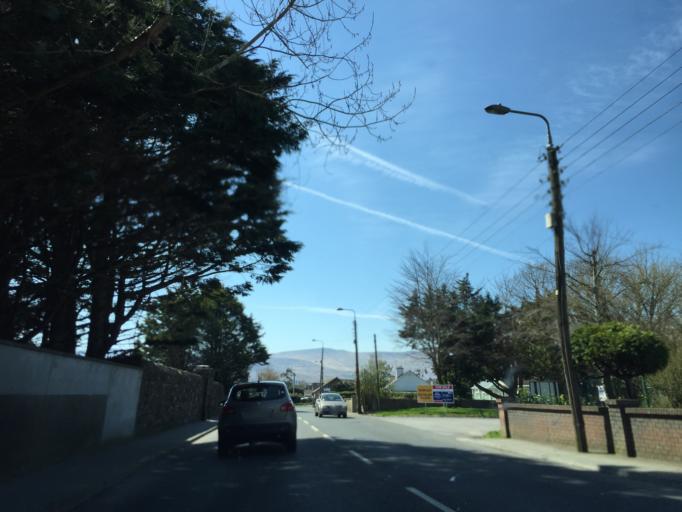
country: IE
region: Munster
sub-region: Ciarrai
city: Tralee
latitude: 52.2612
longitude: -9.6849
